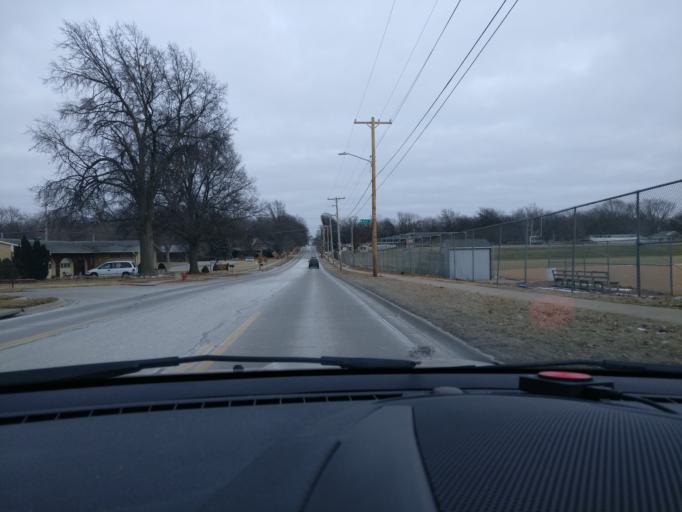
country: US
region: Nebraska
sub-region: Lancaster County
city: Lincoln
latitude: 40.8425
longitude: -96.6375
